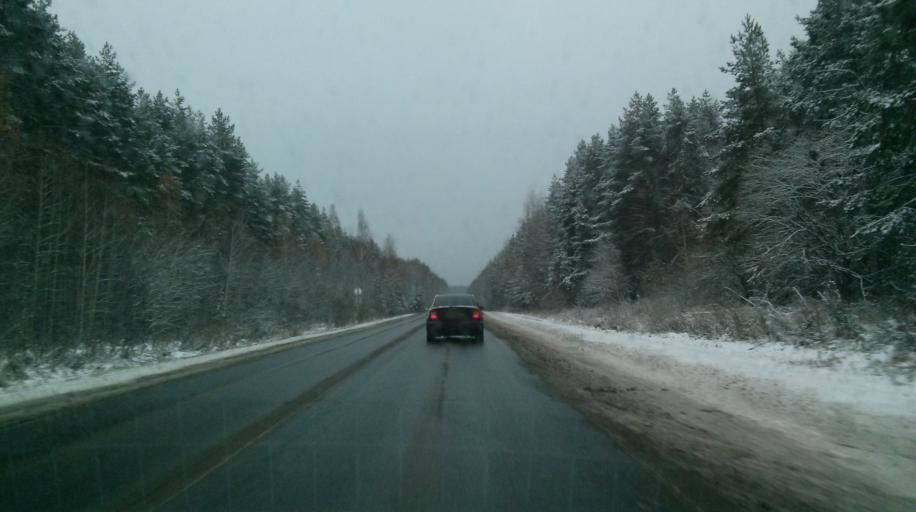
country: RU
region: Nizjnij Novgorod
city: Vorsma
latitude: 56.0235
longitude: 43.3545
